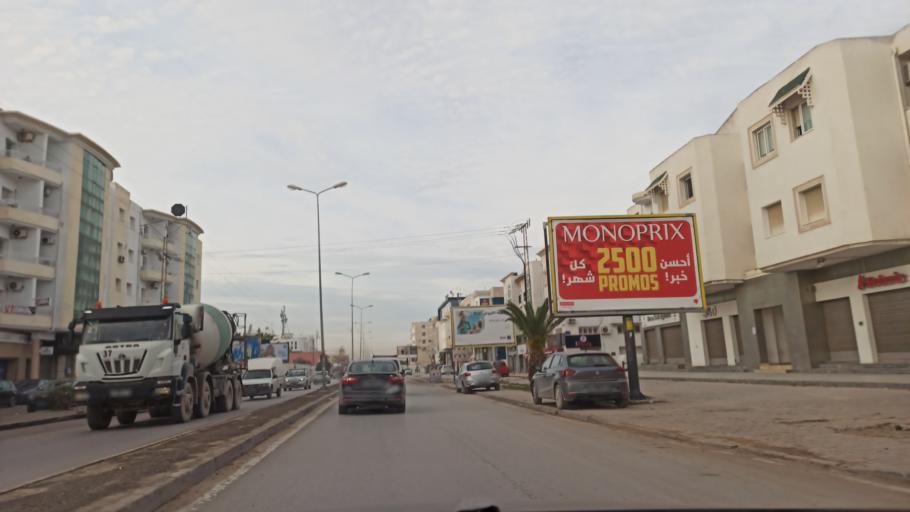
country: TN
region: Ariana
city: Ariana
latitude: 36.8649
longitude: 10.2178
